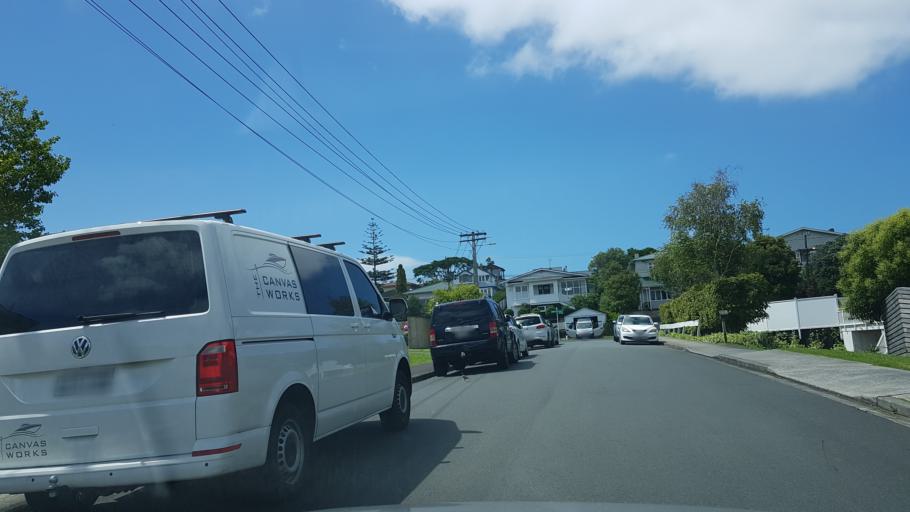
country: NZ
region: Auckland
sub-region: Auckland
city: North Shore
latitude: -36.8140
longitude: 174.7464
